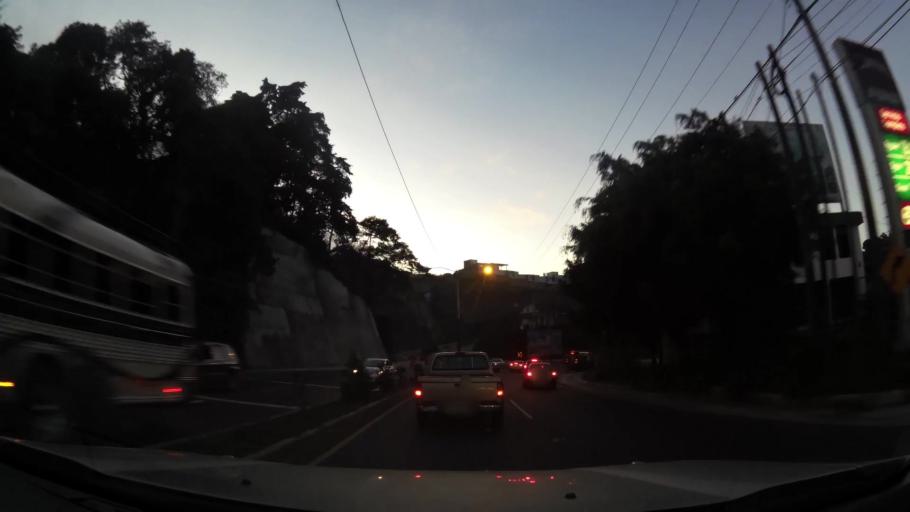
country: GT
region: Guatemala
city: Mixco
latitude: 14.6313
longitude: -90.6007
